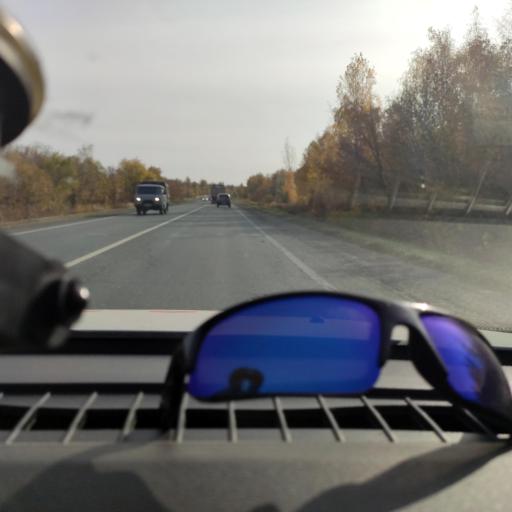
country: RU
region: Samara
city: Chapayevsk
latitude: 52.9926
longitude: 49.8307
